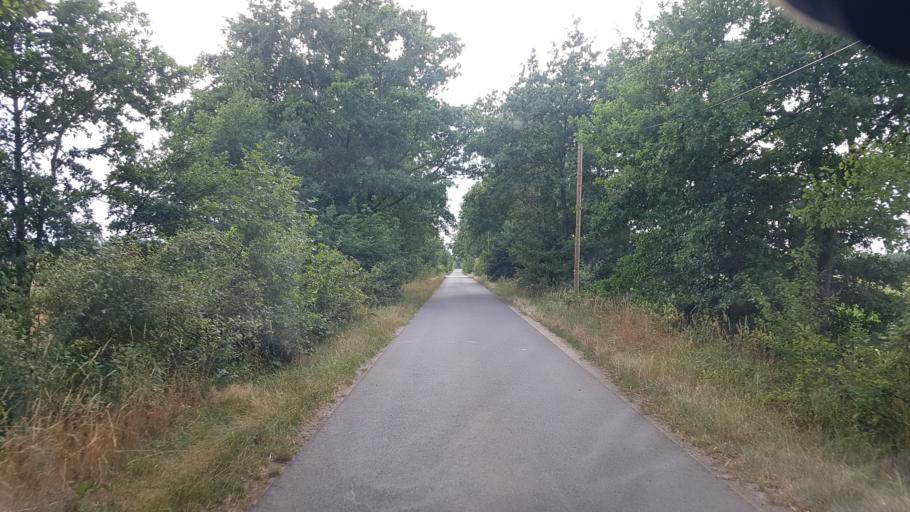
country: DE
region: Brandenburg
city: Groden
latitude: 51.4424
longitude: 13.5688
